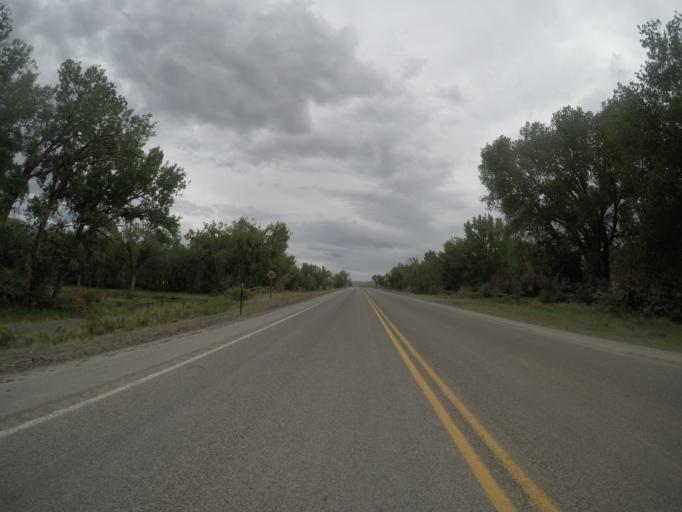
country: US
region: Wyoming
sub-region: Big Horn County
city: Lovell
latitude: 44.8612
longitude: -108.3316
